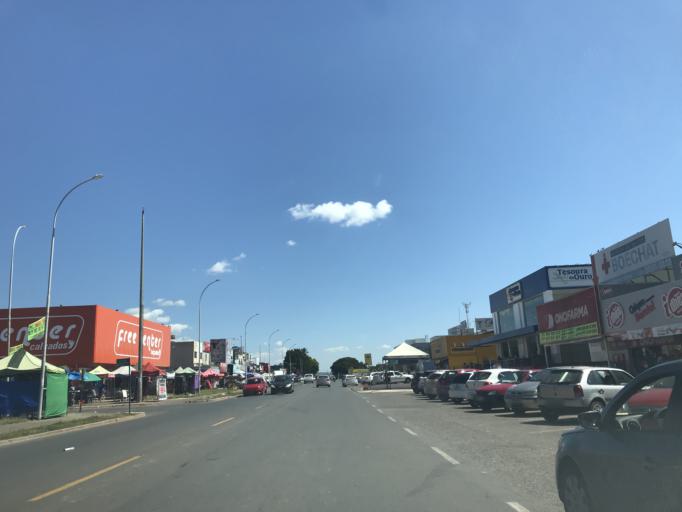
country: BR
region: Federal District
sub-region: Brasilia
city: Brasilia
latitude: -15.6503
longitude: -47.7895
